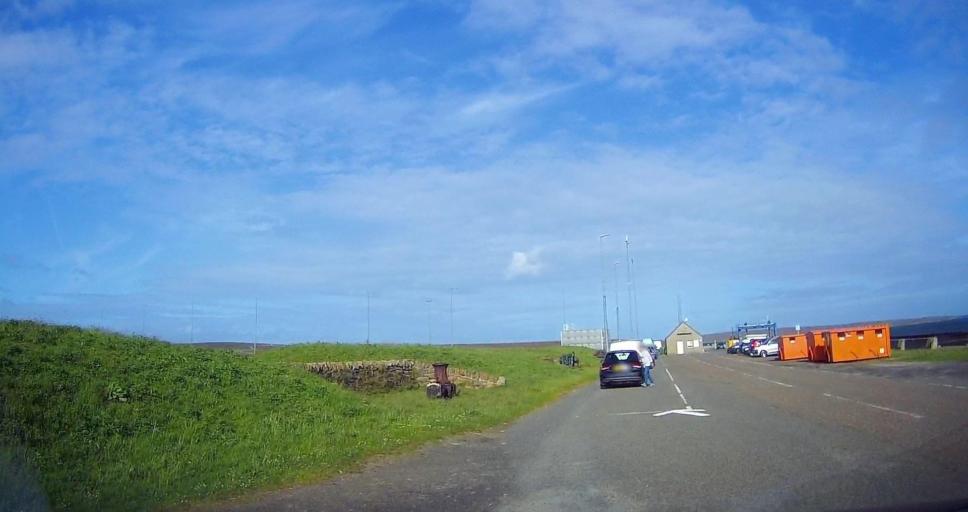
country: GB
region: Scotland
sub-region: Orkney Islands
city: Stromness
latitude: 58.8339
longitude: -3.1945
